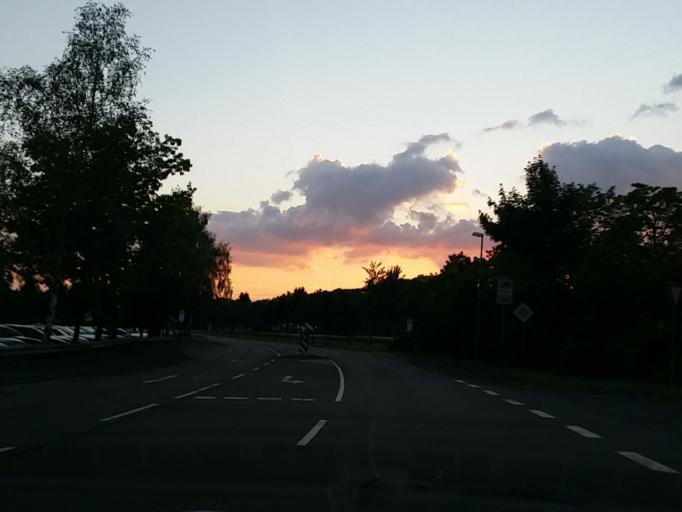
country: DE
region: Saarland
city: Wadern
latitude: 49.5265
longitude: 6.9072
